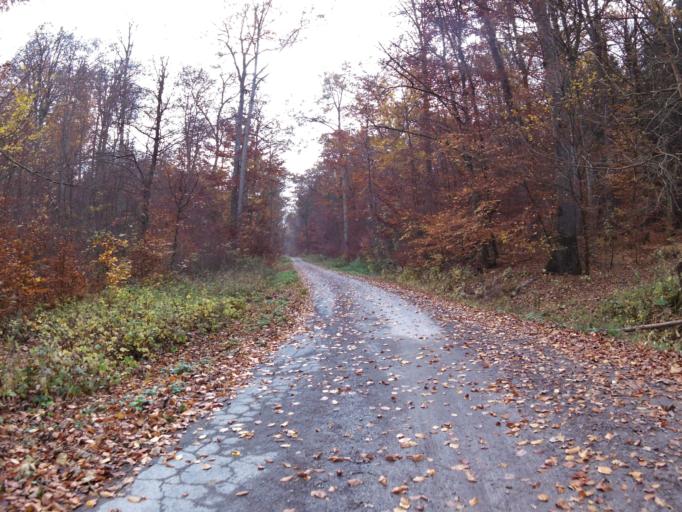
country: DE
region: Bavaria
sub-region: Regierungsbezirk Unterfranken
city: Waldbrunn
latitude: 49.7426
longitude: 9.8115
